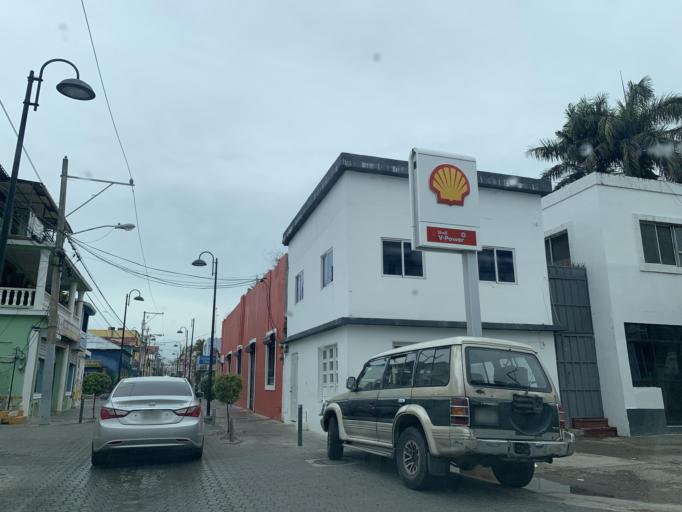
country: DO
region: Puerto Plata
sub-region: Puerto Plata
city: Puerto Plata
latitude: 19.7991
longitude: -70.6952
